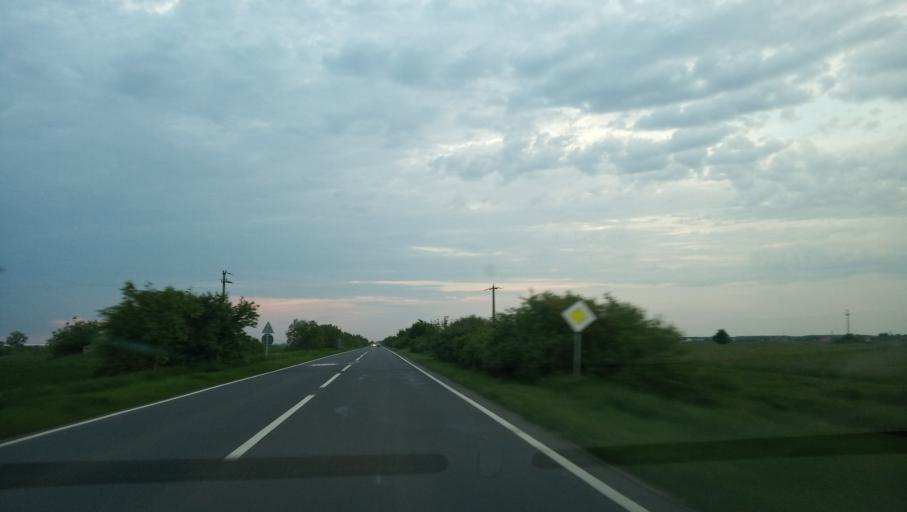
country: RO
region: Timis
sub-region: Comuna Padureni
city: Padureni
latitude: 45.5887
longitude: 21.2004
